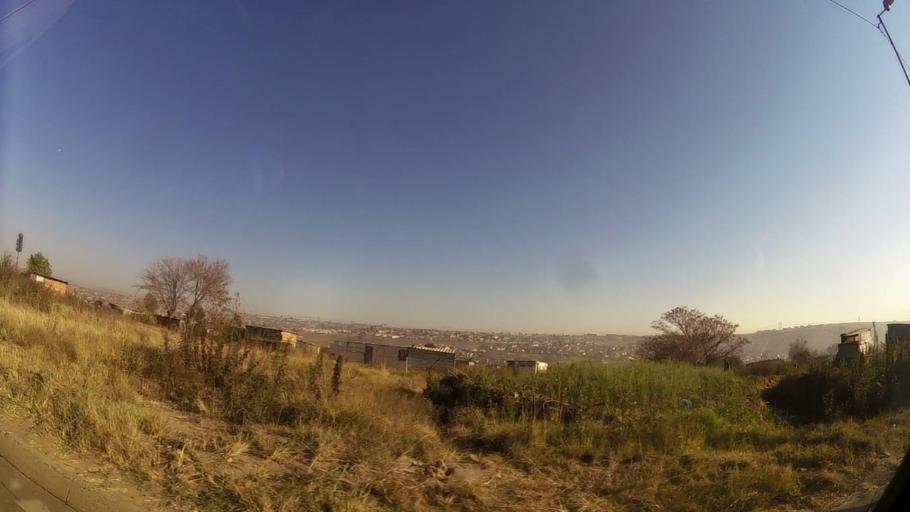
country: ZA
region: Gauteng
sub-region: City of Johannesburg Metropolitan Municipality
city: Midrand
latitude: -25.9171
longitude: 28.1053
